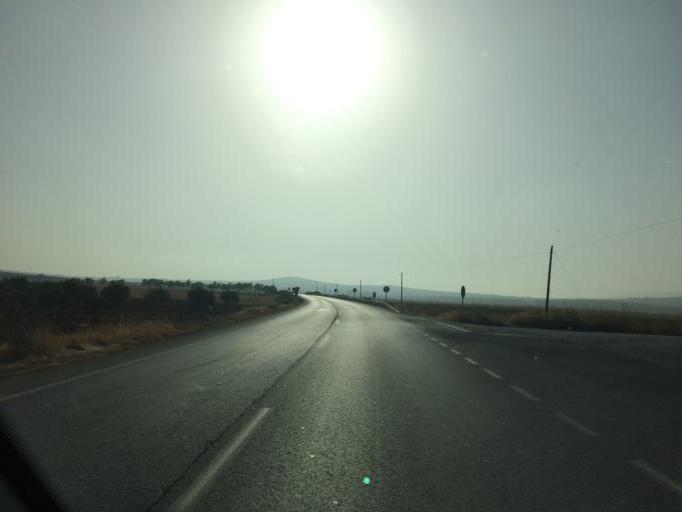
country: ES
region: Andalusia
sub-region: Provincia de Malaga
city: Humilladero
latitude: 37.0621
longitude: -4.7094
